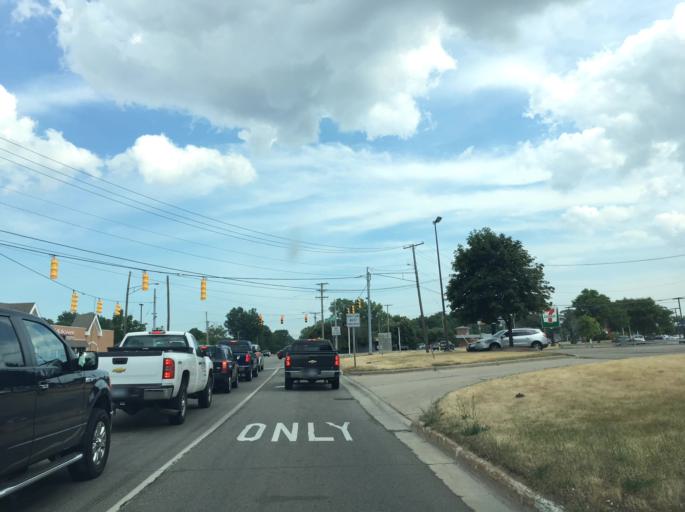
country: US
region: Michigan
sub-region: Macomb County
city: Utica
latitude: 42.6116
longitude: -83.0323
